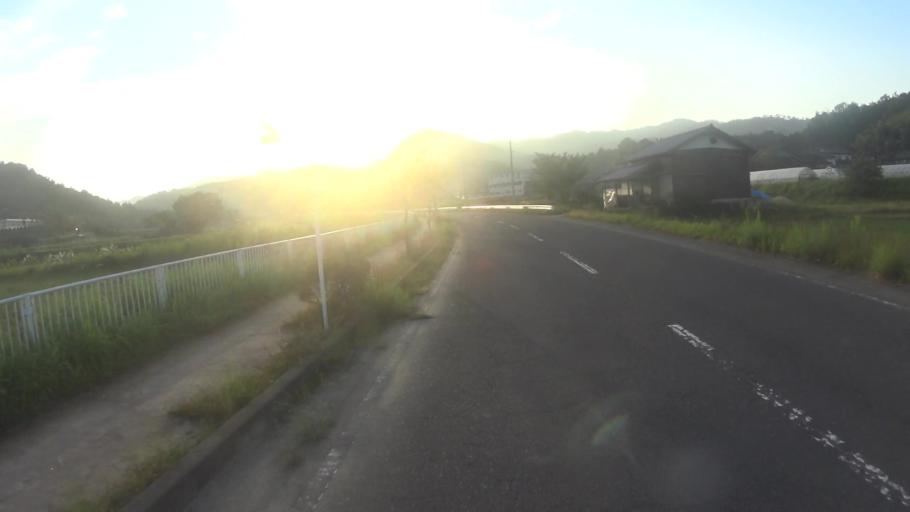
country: JP
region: Kyoto
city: Miyazu
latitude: 35.5681
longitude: 135.0918
